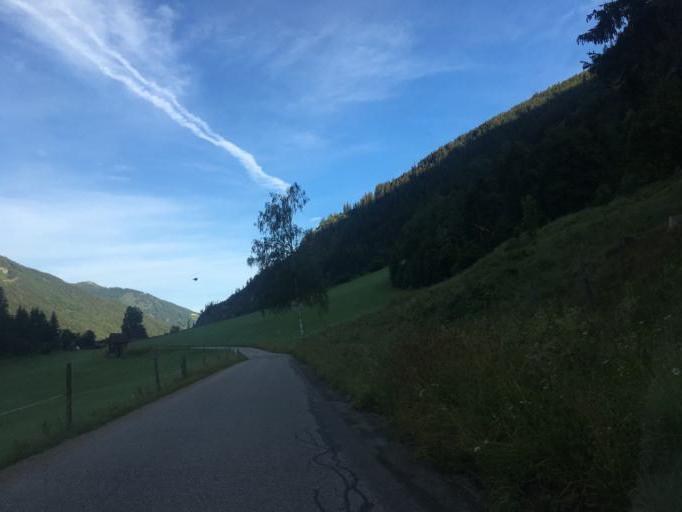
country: AT
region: Styria
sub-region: Politischer Bezirk Liezen
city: Schladming
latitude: 47.3551
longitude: 13.7184
